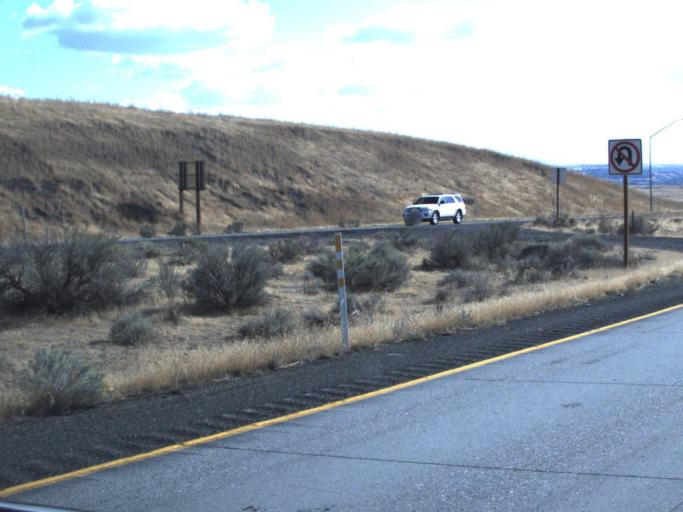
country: US
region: Oregon
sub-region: Umatilla County
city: Umatilla
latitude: 45.9685
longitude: -119.3409
